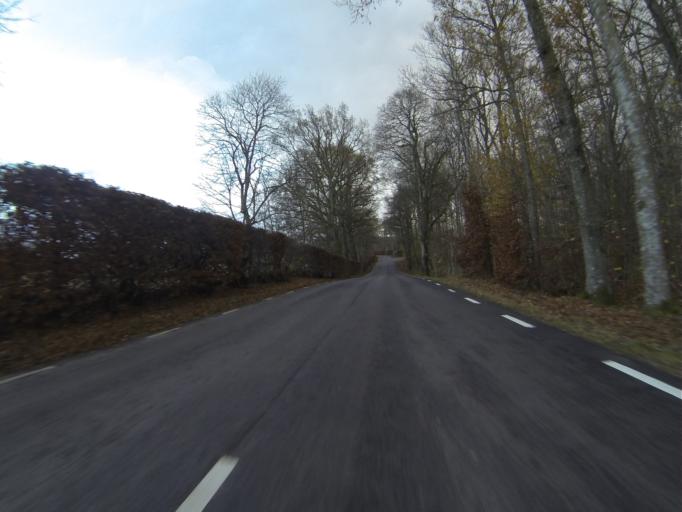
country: SE
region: Skane
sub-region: Lunds Kommun
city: Genarp
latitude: 55.5850
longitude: 13.4218
